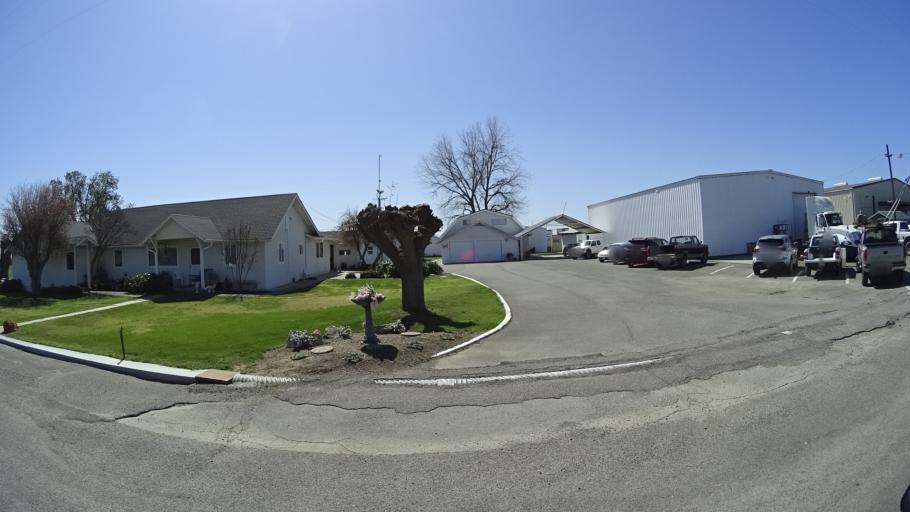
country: US
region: California
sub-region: Glenn County
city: Orland
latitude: 39.7897
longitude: -122.1072
